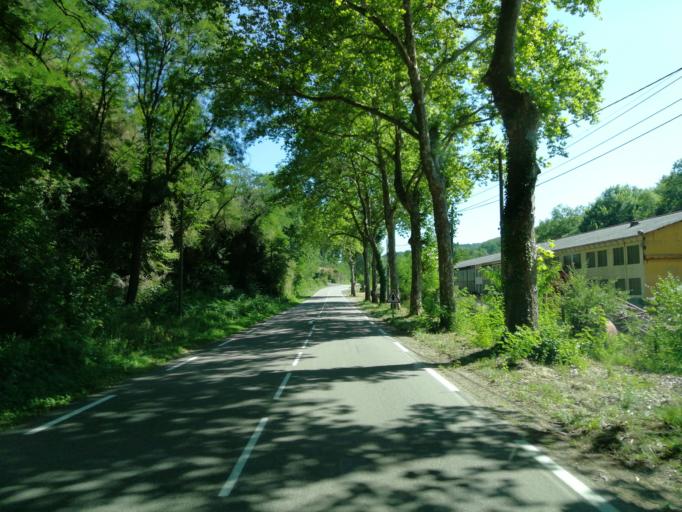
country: FR
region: Limousin
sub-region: Departement de la Correze
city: Brive-la-Gaillarde
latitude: 45.1274
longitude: 1.5172
